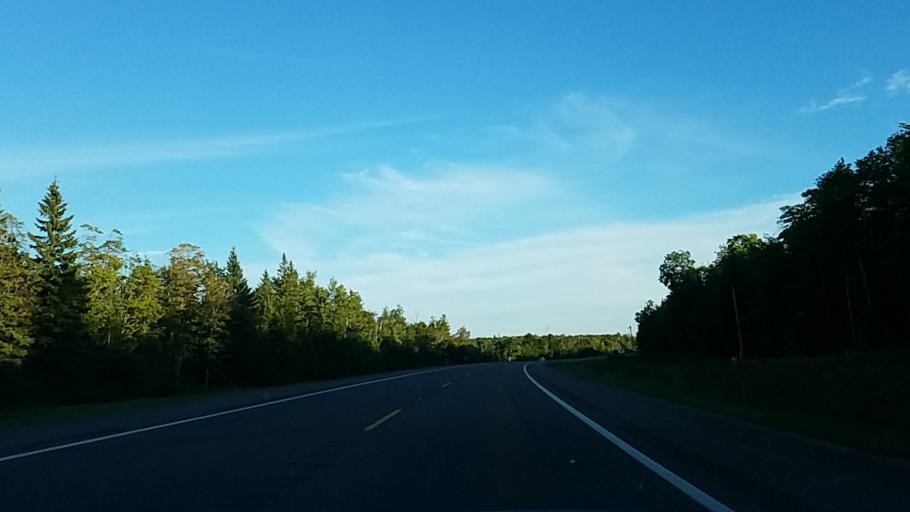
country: US
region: Michigan
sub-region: Alger County
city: Munising
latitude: 46.4574
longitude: -86.8916
